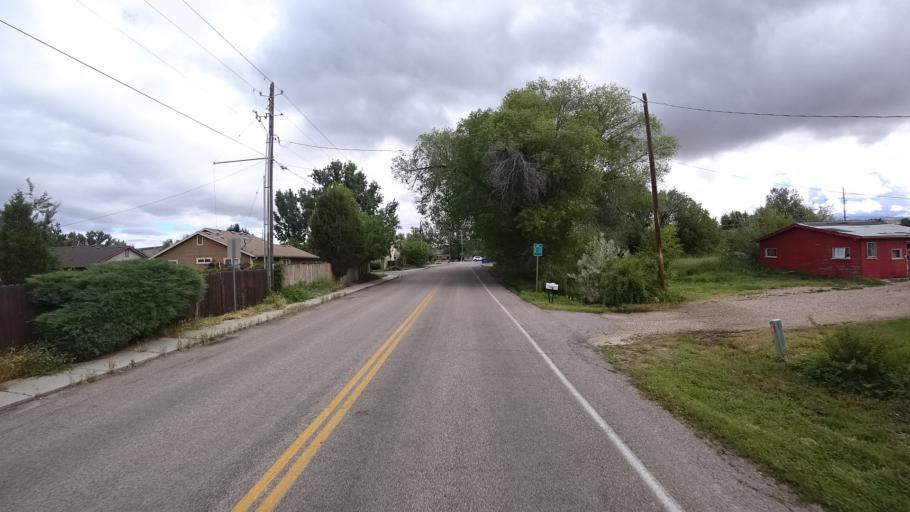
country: US
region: Idaho
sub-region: Ada County
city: Eagle
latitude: 43.6760
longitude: -116.2990
